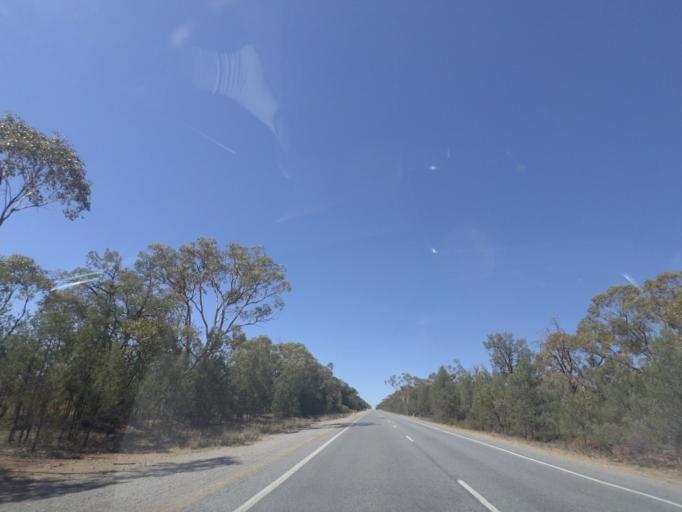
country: AU
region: New South Wales
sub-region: Narrandera
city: Narrandera
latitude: -34.4268
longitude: 146.8440
